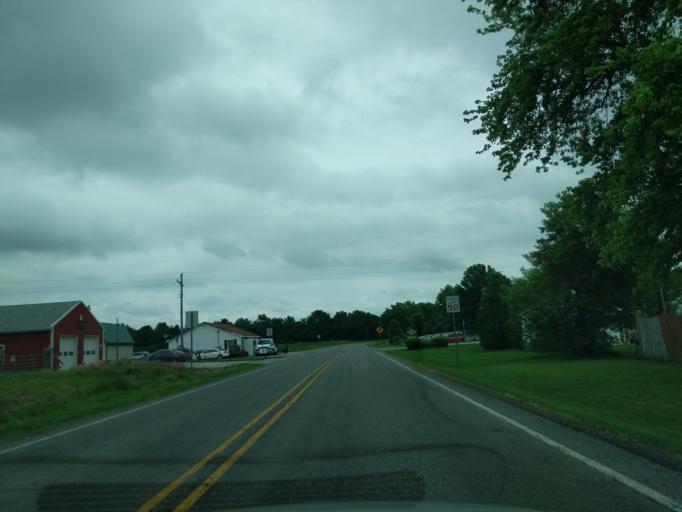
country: US
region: Indiana
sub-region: Tipton County
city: Tipton
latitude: 40.2852
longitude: -85.9482
